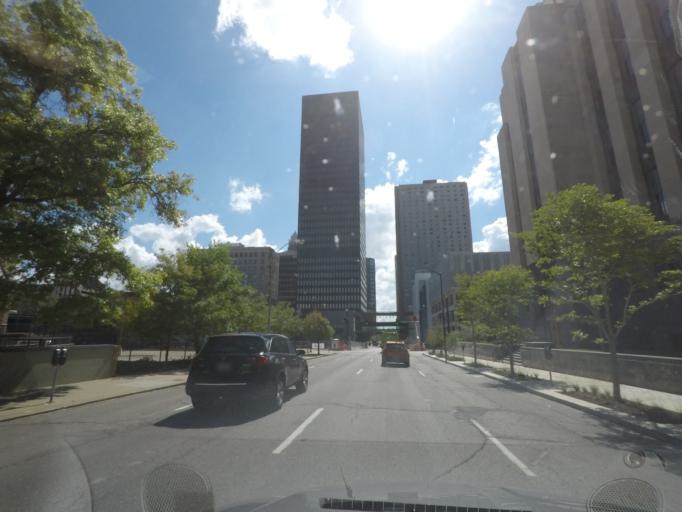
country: US
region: Iowa
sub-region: Polk County
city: Des Moines
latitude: 41.5888
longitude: -93.6270
